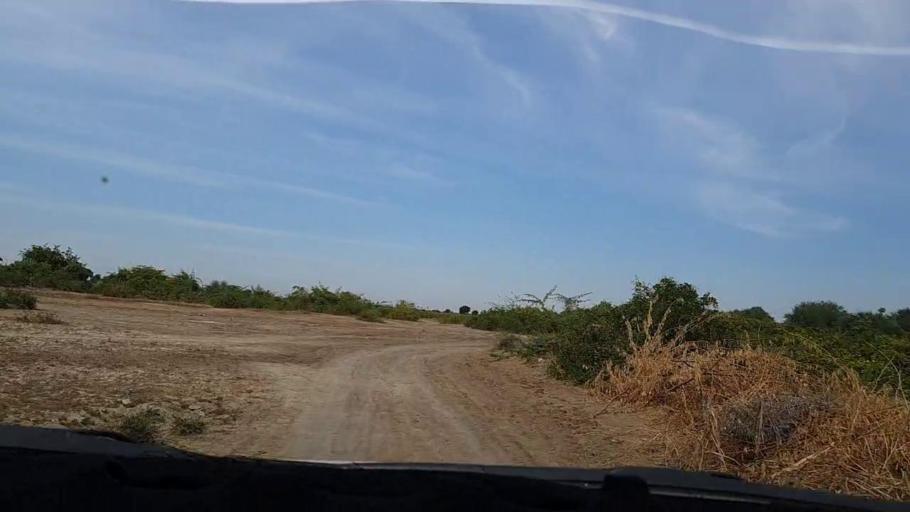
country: PK
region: Sindh
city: Dhoro Naro
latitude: 25.4736
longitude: 69.4750
